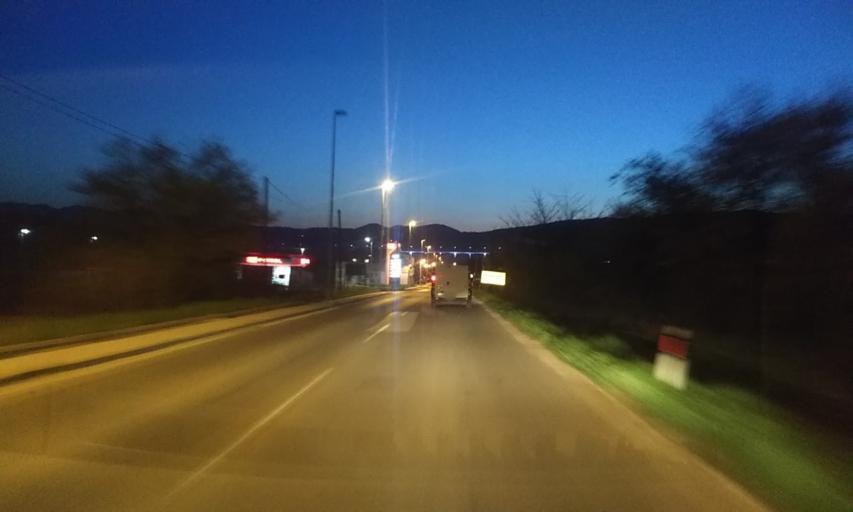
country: RS
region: Central Serbia
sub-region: Pcinjski Okrug
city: Vladicin Han
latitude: 42.7108
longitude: 22.0979
